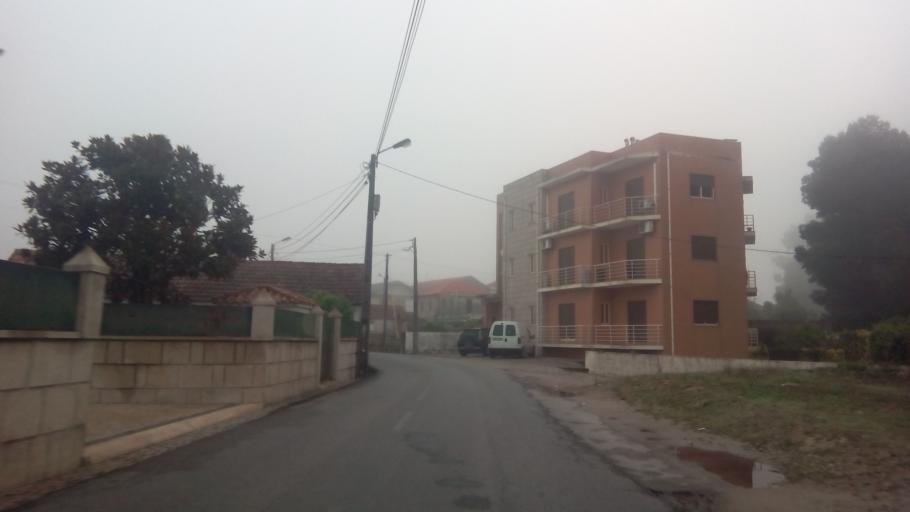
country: PT
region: Porto
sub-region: Paredes
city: Paredes
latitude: 41.2111
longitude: -8.3191
